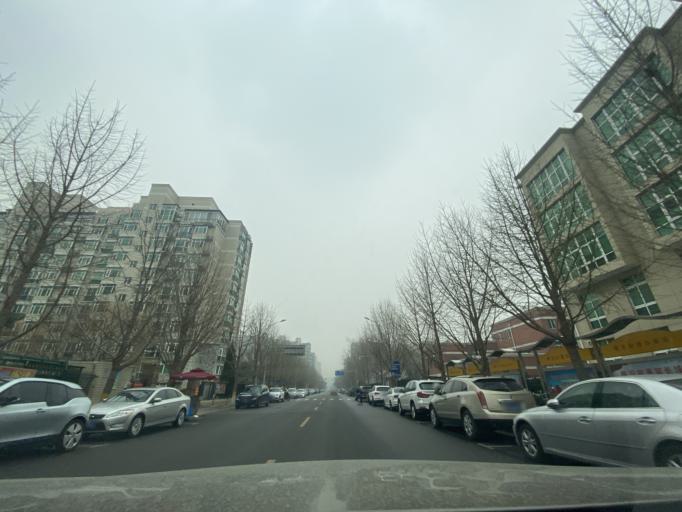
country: CN
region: Beijing
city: Sijiqing
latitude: 39.9643
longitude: 116.2738
